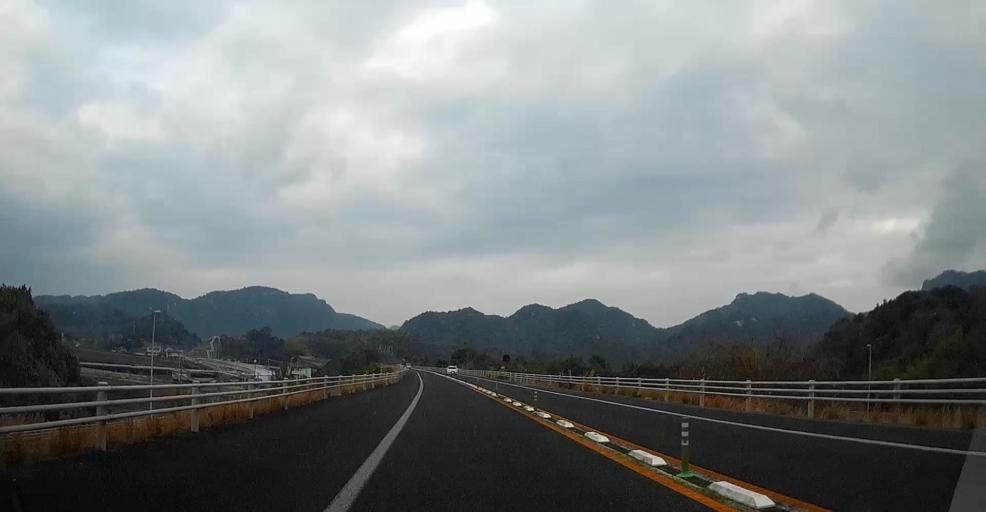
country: JP
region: Kumamoto
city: Hondo
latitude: 32.4966
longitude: 130.3909
